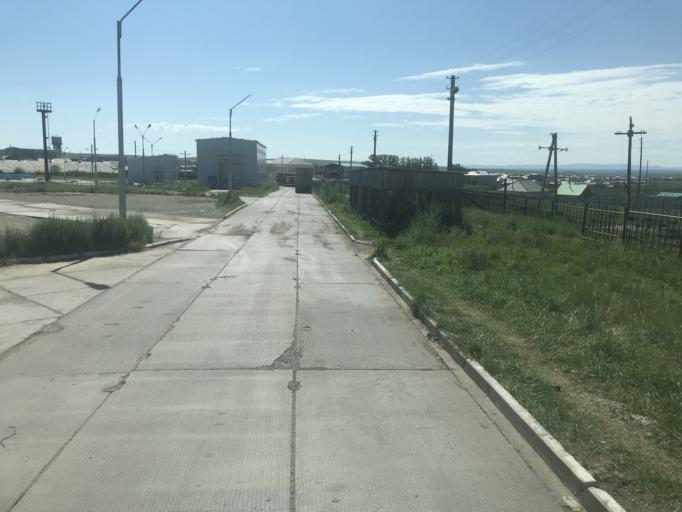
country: MN
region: Selenge
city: Altanbulag
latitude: 50.3213
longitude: 106.4883
